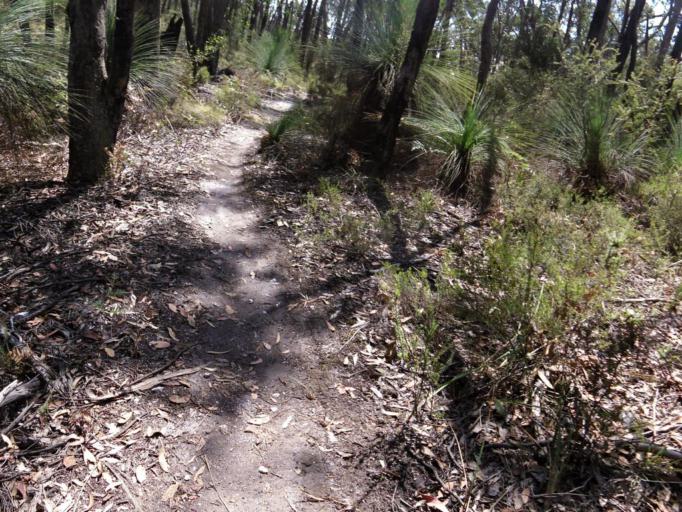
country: AU
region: Victoria
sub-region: Melton
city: Melton West
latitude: -37.5172
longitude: 144.5555
